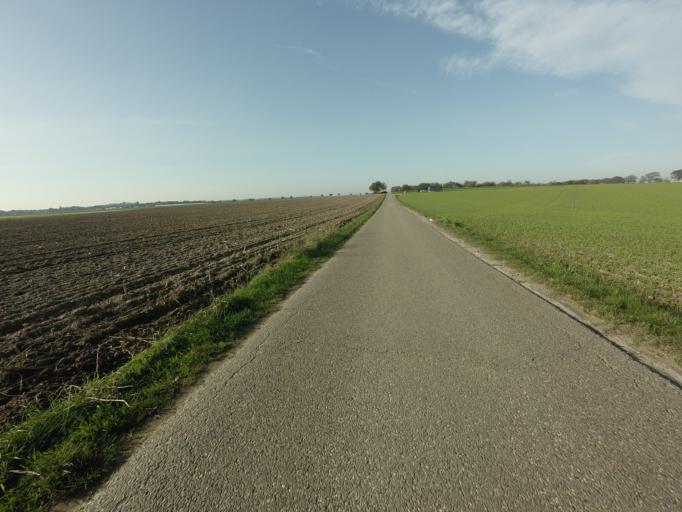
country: DE
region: North Rhine-Westphalia
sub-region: Regierungsbezirk Koln
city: Selfkant
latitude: 51.0387
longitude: 5.9354
